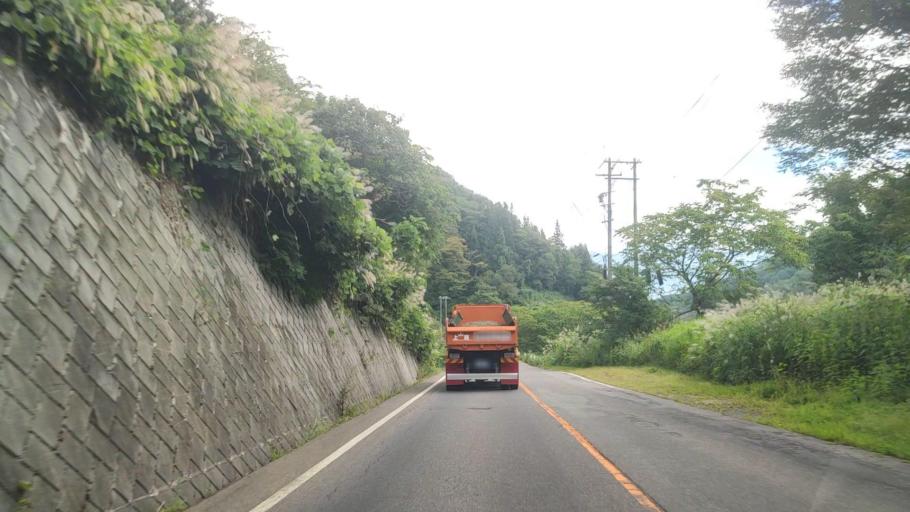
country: JP
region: Nagano
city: Iiyama
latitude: 36.8680
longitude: 138.3270
